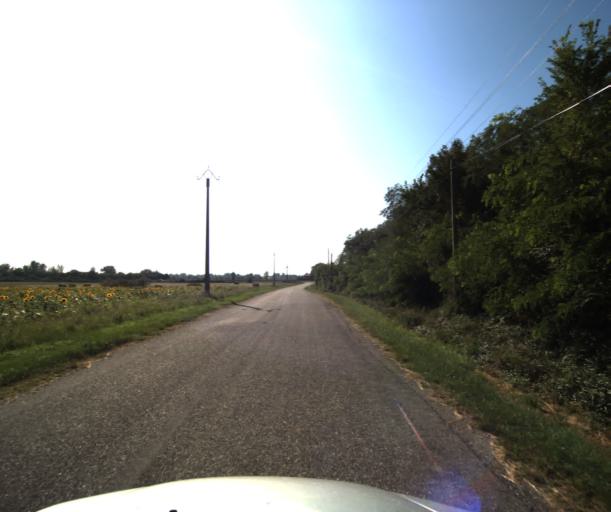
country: FR
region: Midi-Pyrenees
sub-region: Departement de la Haute-Garonne
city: Le Fauga
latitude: 43.4222
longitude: 1.3052
